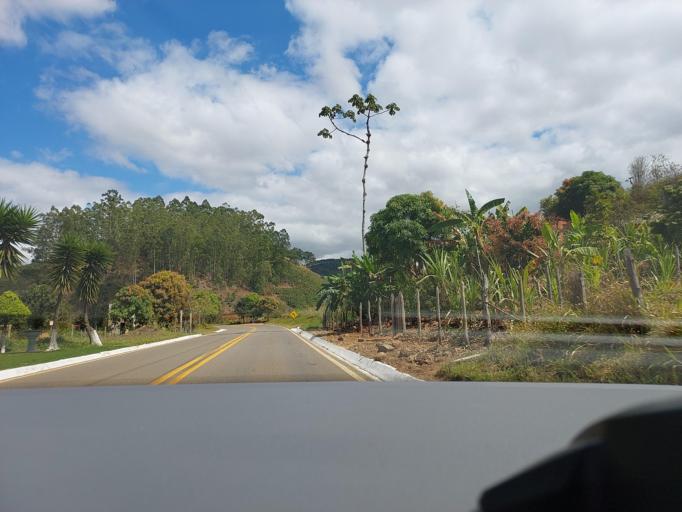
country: BR
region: Minas Gerais
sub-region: Mirai
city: Mirai
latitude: -21.0034
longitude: -42.5519
